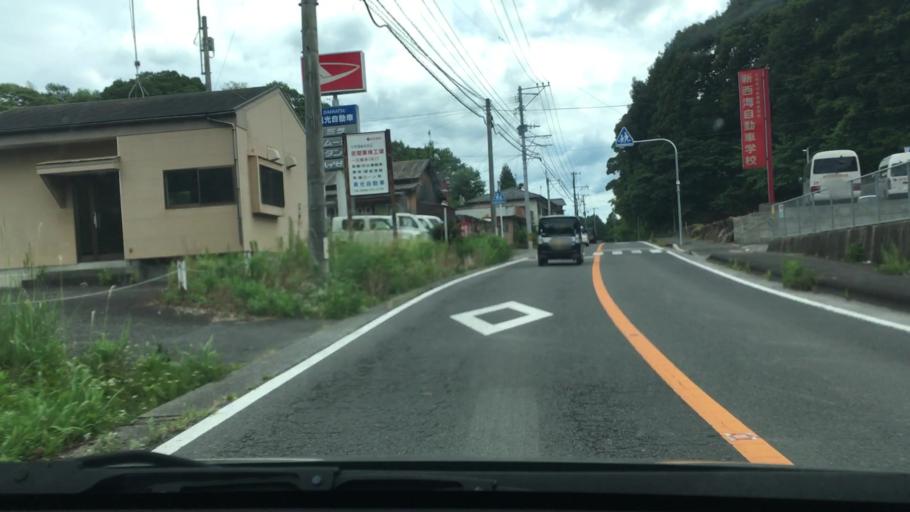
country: JP
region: Nagasaki
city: Togitsu
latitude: 32.9817
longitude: 129.7815
